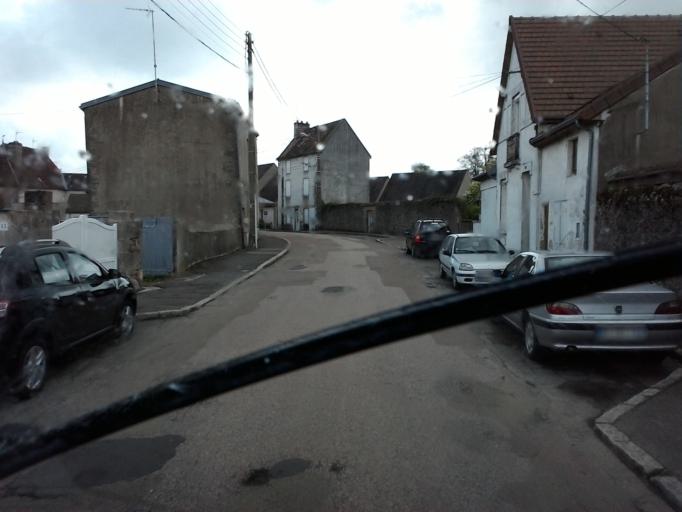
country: FR
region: Bourgogne
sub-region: Departement de la Cote-d'Or
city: Saulieu
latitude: 47.2783
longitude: 4.2286
